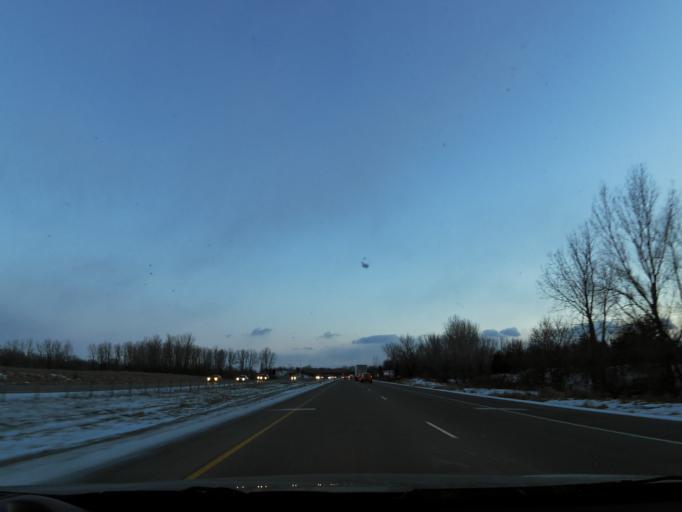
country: US
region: Minnesota
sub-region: Ramsey County
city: North Saint Paul
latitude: 45.0106
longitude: -92.9584
